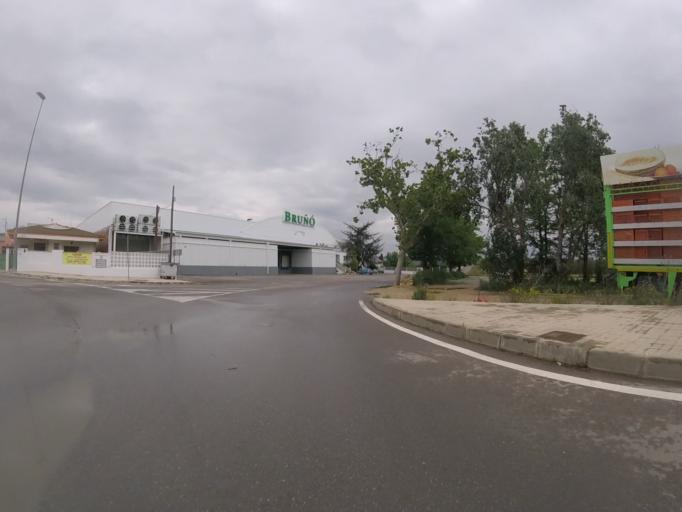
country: ES
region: Valencia
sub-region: Provincia de Castello
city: Alcala de Xivert
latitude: 40.3101
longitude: 0.2299
